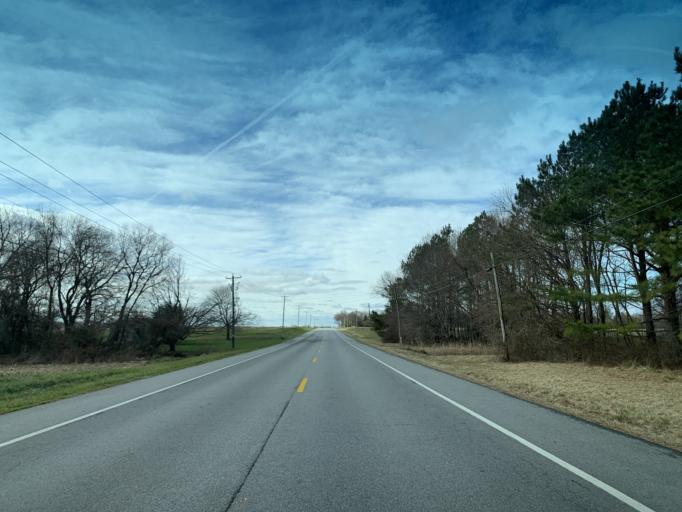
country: US
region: Maryland
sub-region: Queen Anne's County
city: Kingstown
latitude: 39.3229
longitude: -76.0112
